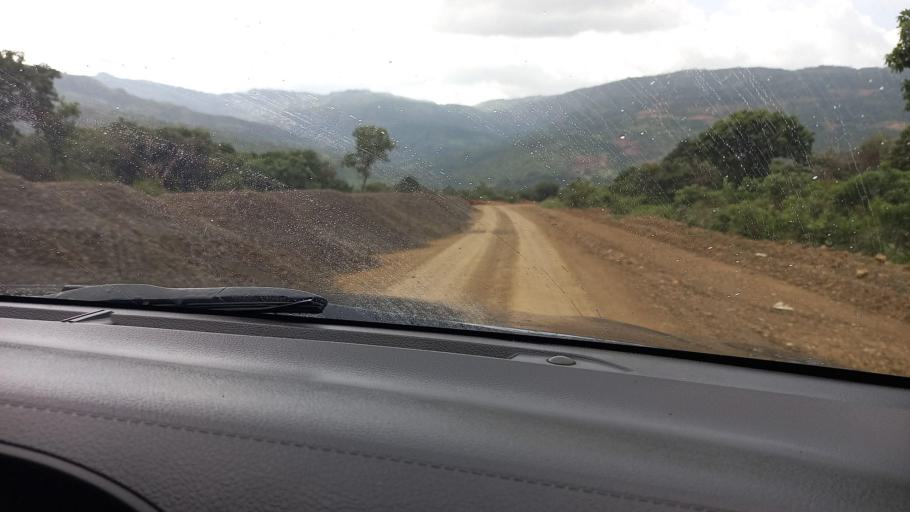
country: ET
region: Southern Nations, Nationalities, and People's Region
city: Mizan Teferi
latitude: 6.1872
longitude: 35.6887
